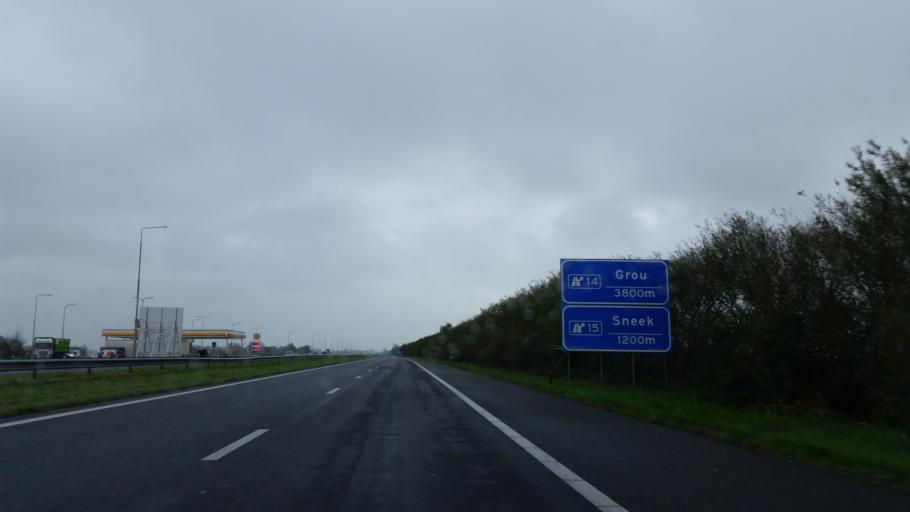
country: NL
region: Friesland
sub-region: Gemeente Leeuwarden
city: Wirdum
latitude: 53.1299
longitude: 5.8031
